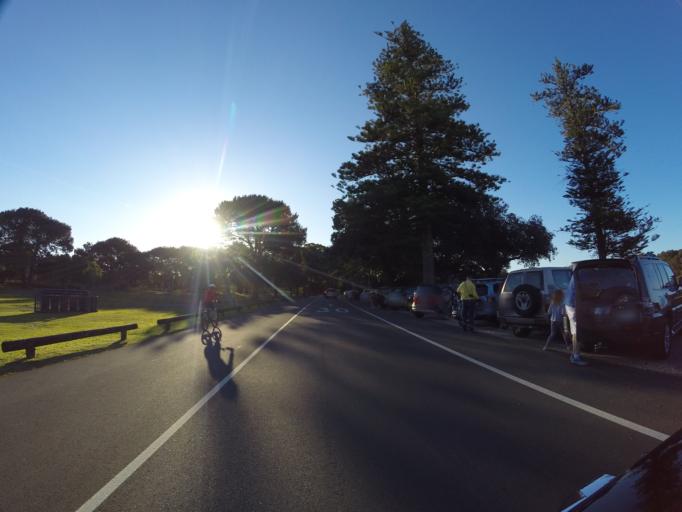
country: AU
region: New South Wales
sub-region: Woollahra
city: Woollahra
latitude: -33.9016
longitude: 151.2286
